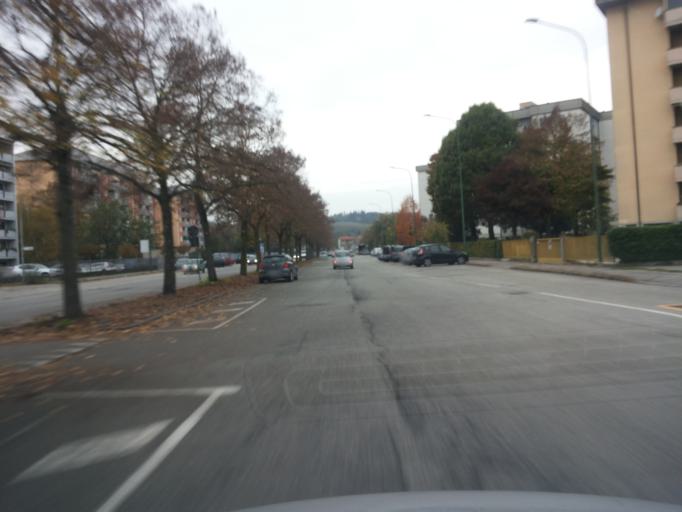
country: IT
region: Piedmont
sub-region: Provincia di Alessandria
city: Casale Monferrato
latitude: 45.1237
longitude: 8.4577
